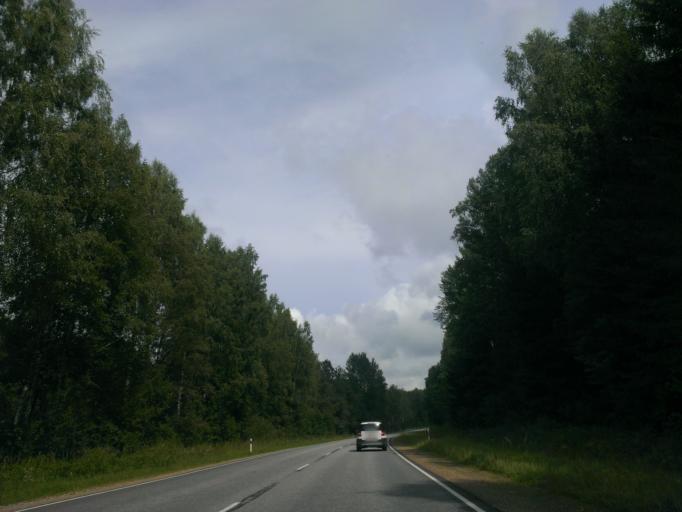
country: LV
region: Ligatne
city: Ligatne
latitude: 57.1814
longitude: 24.9897
